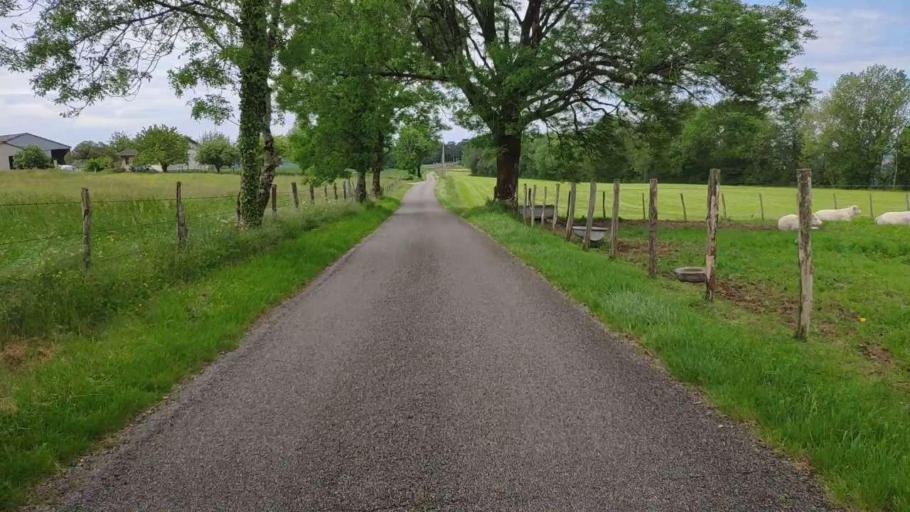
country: FR
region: Franche-Comte
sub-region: Departement du Jura
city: Poligny
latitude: 46.7597
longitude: 5.6369
